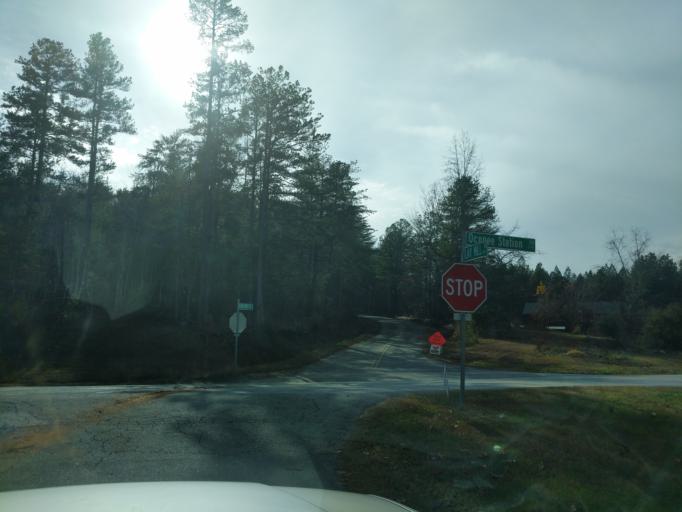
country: US
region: South Carolina
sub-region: Oconee County
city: Walhalla
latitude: 34.8412
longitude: -83.0551
